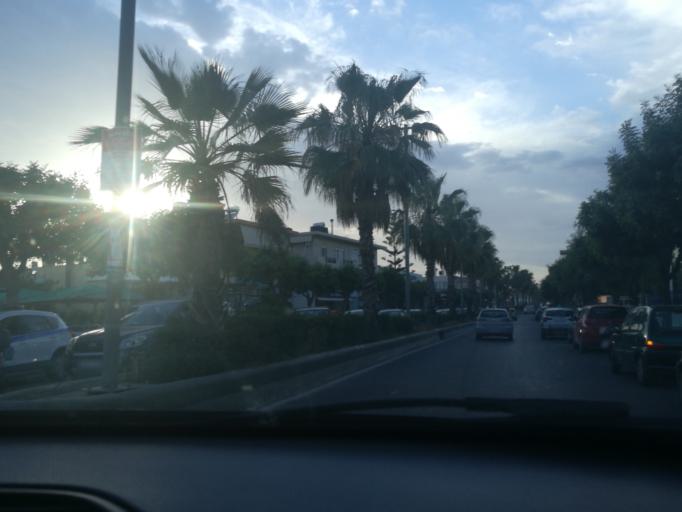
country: GR
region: Crete
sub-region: Nomos Irakleiou
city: Irakleion
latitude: 35.3152
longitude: 25.1476
